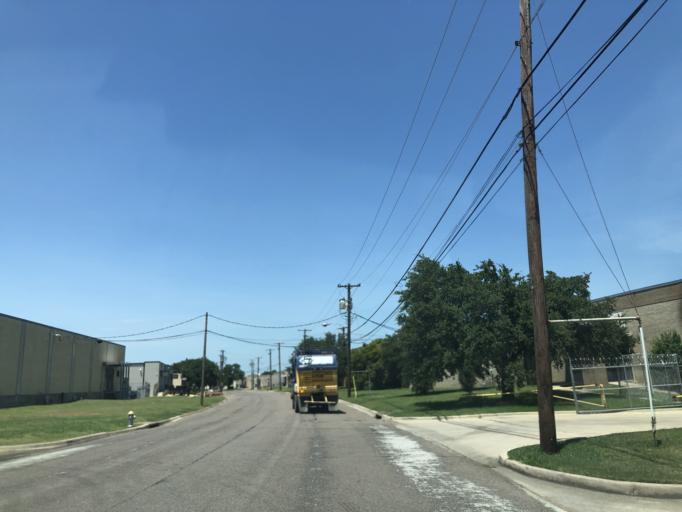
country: US
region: Texas
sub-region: Dallas County
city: Irving
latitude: 32.8314
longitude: -96.8845
